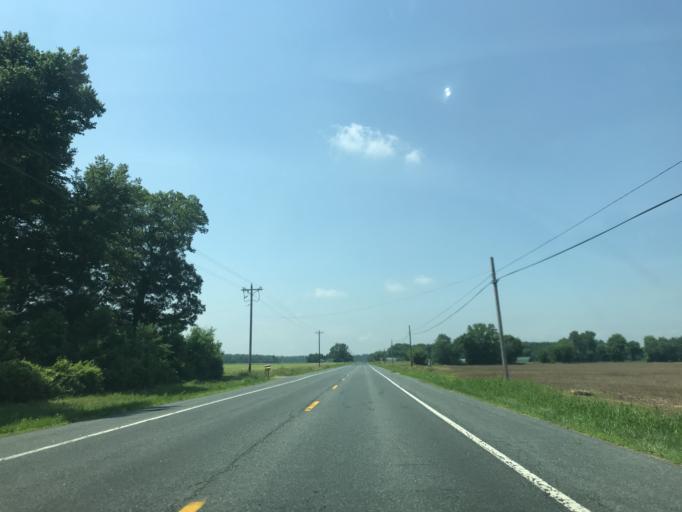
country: US
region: Maryland
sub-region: Caroline County
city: Federalsburg
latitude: 38.6485
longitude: -75.7180
